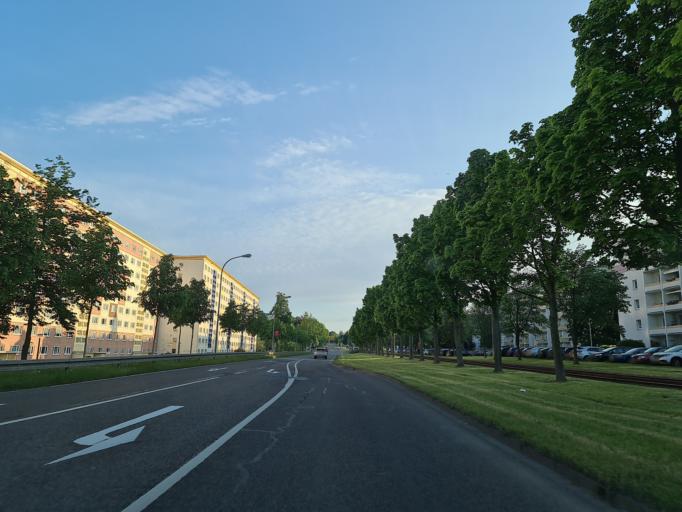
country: DE
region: Saxony
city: Neukirchen
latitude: 50.8073
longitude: 12.8912
